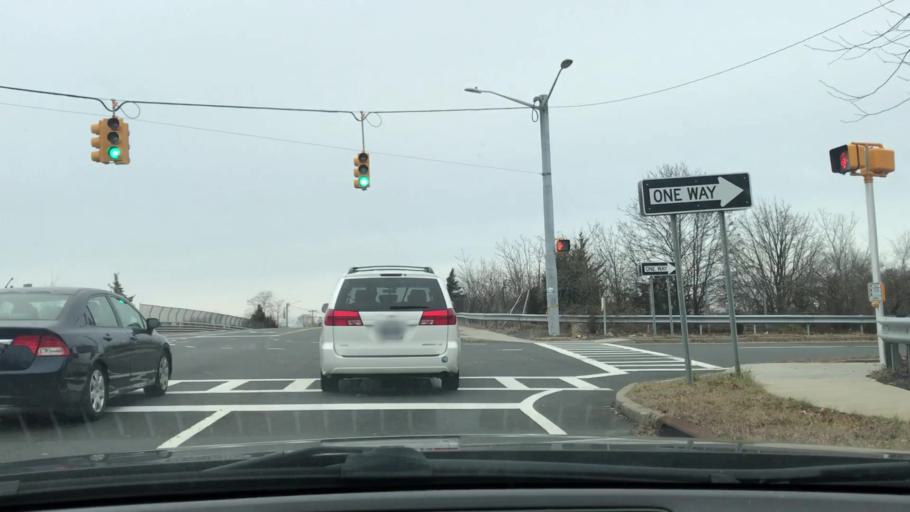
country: US
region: New York
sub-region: Suffolk County
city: North Patchogue
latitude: 40.7780
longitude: -73.0156
